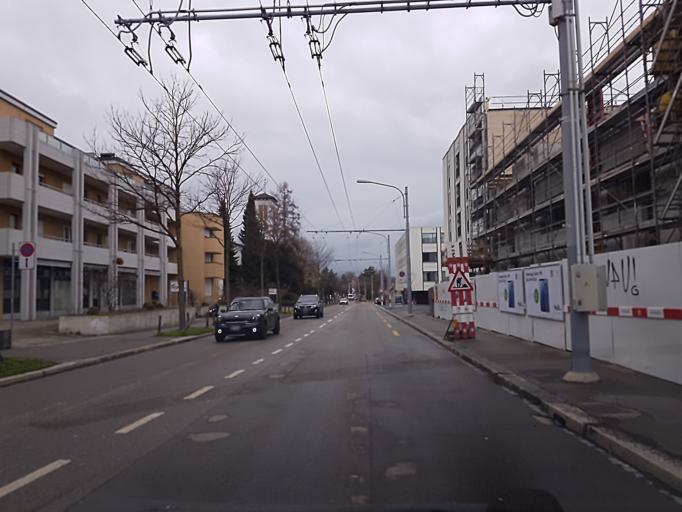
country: CH
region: Zurich
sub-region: Bezirk Zuerich
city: Zuerich (Kreis 3)
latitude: 47.3599
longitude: 8.5071
